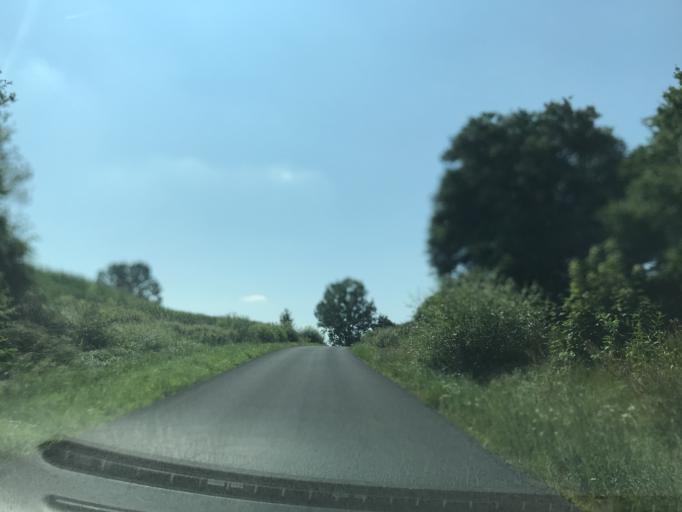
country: PL
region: Kujawsko-Pomorskie
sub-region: Powiat lipnowski
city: Chrostkowo
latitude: 52.9449
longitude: 19.2117
